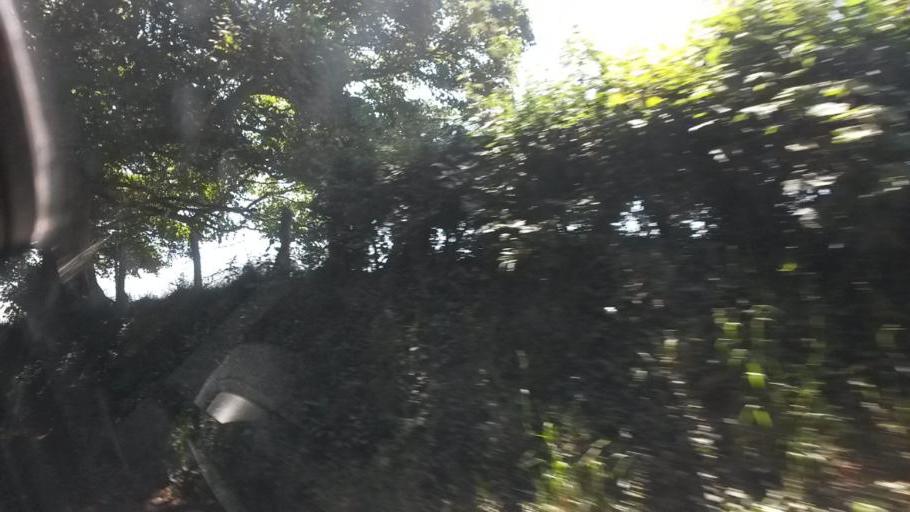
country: IE
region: Leinster
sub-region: An Mhi
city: Ashbourne
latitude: 53.5292
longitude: -6.3244
